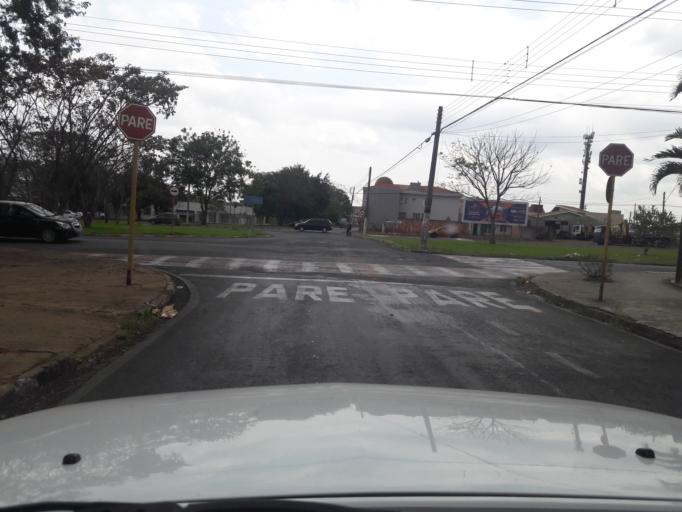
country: BR
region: Sao Paulo
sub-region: Moji-Guacu
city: Mogi-Gaucu
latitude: -22.3464
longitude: -46.9395
